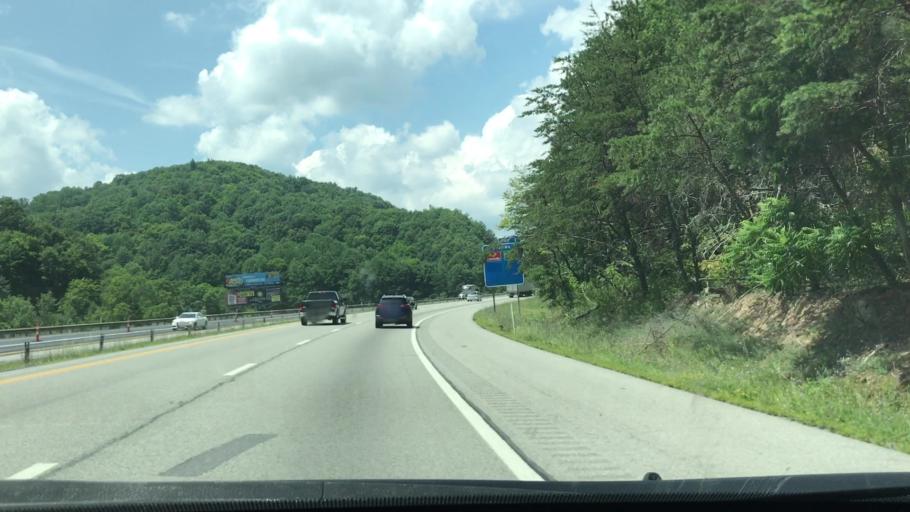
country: US
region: West Virginia
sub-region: Mercer County
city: Princeton
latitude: 37.2960
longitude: -81.1038
